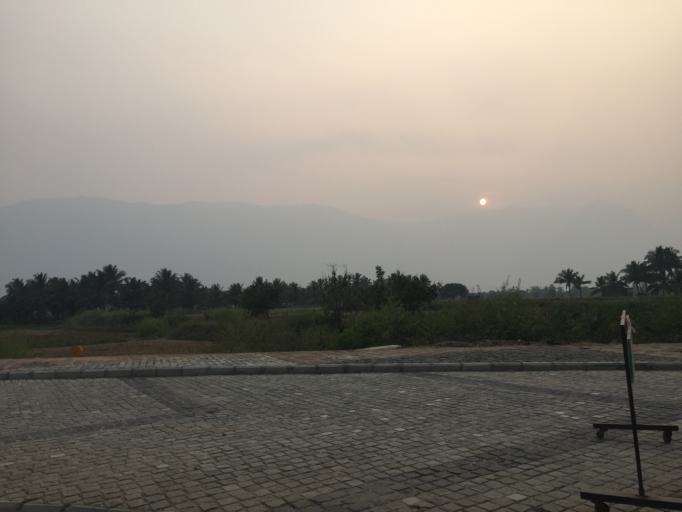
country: IN
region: Tamil Nadu
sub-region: Coimbatore
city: Perur
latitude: 10.9638
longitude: 76.7420
